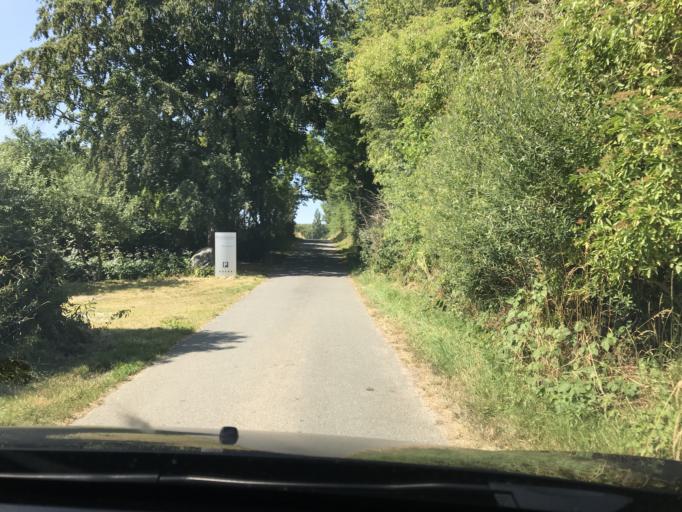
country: DK
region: South Denmark
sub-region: AEro Kommune
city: AEroskobing
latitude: 54.9101
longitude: 10.3210
